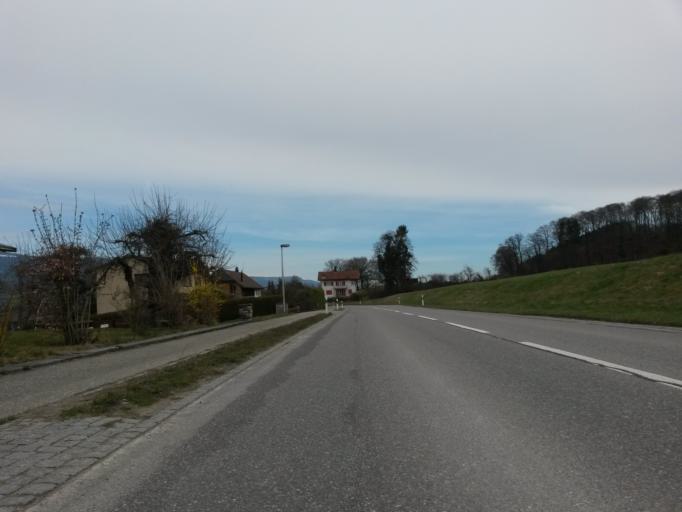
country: CH
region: Bern
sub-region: Seeland District
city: Arch
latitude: 47.1713
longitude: 7.4360
